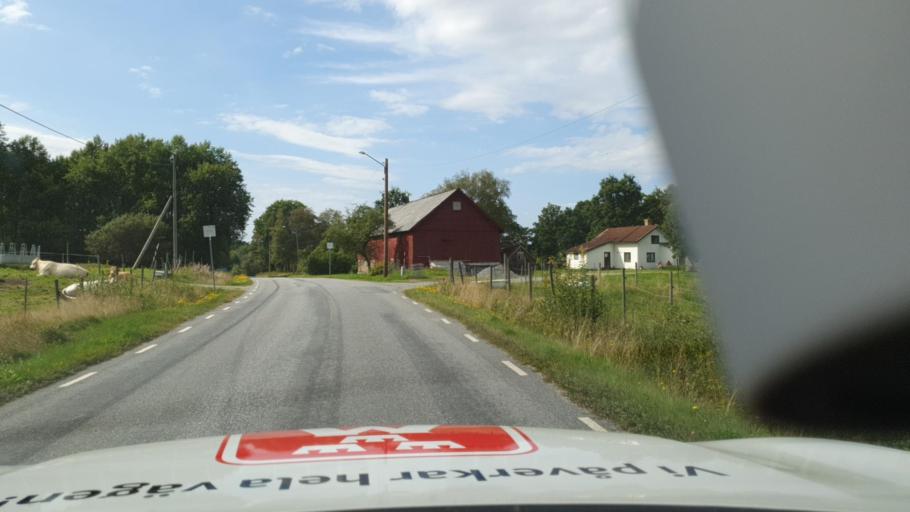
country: SE
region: Vaestra Goetaland
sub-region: Marks Kommun
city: Kinna
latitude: 57.3945
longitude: 12.7944
